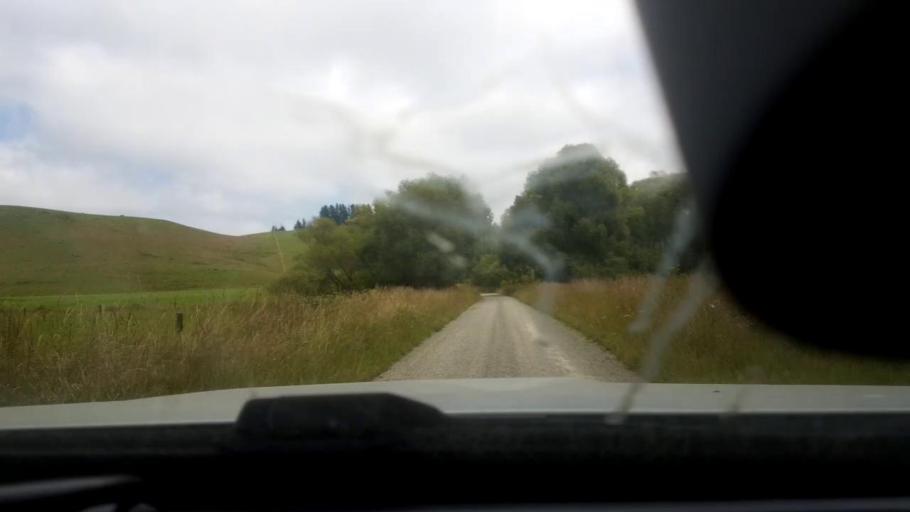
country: NZ
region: Canterbury
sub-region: Timaru District
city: Pleasant Point
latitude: -44.1547
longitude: 171.0948
